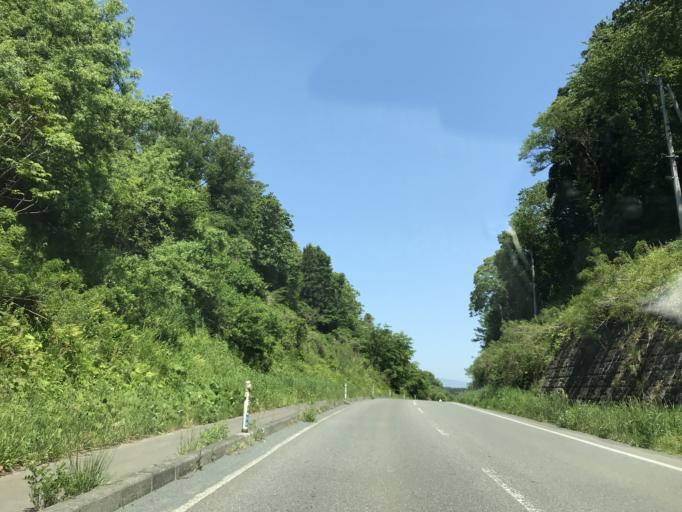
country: JP
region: Iwate
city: Mizusawa
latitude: 39.1716
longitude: 141.0833
